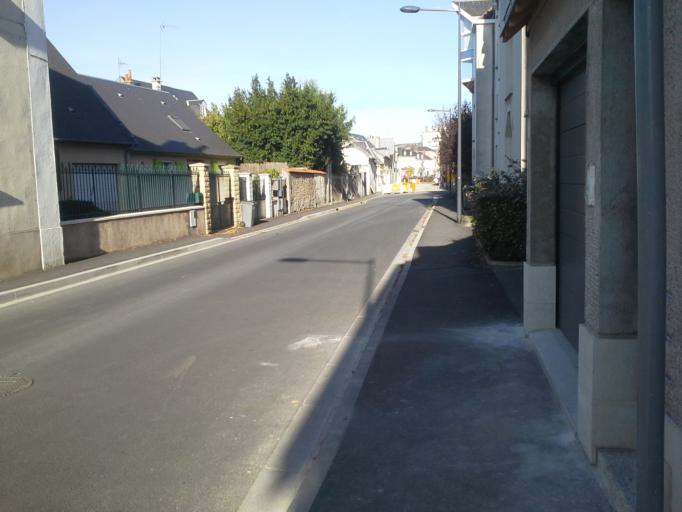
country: FR
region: Centre
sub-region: Departement d'Indre-et-Loire
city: La Riche
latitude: 47.3896
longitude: 0.6649
